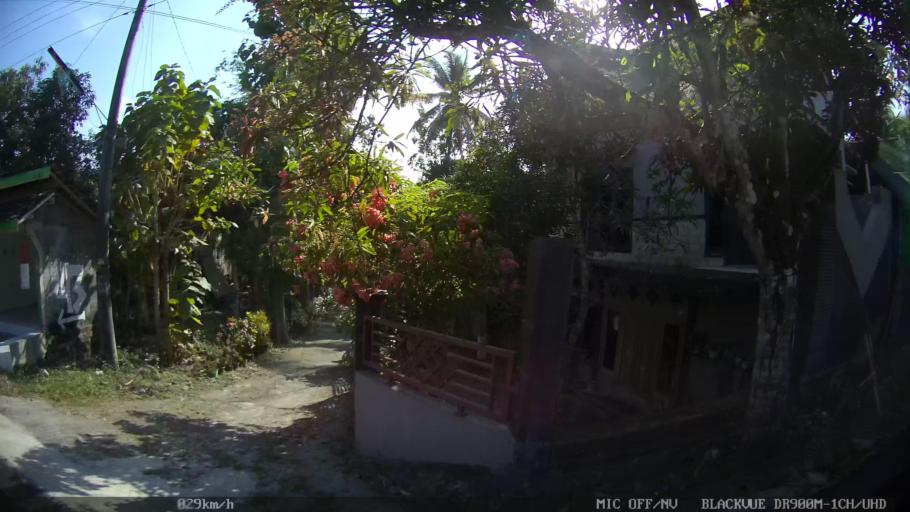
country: ID
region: Daerah Istimewa Yogyakarta
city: Kasihan
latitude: -7.8255
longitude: 110.2733
